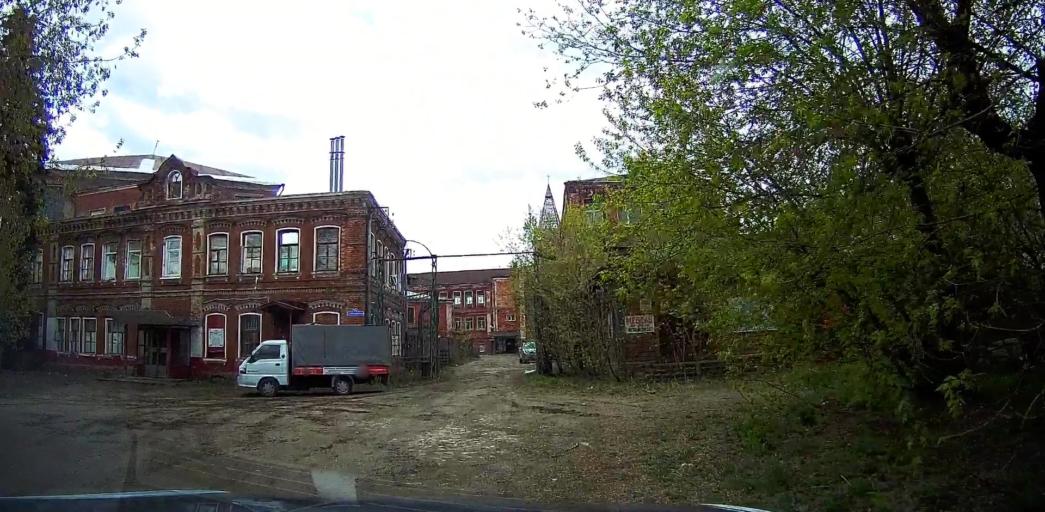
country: RU
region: Moskovskaya
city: Pavlovskiy Posad
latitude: 55.7851
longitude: 38.6867
